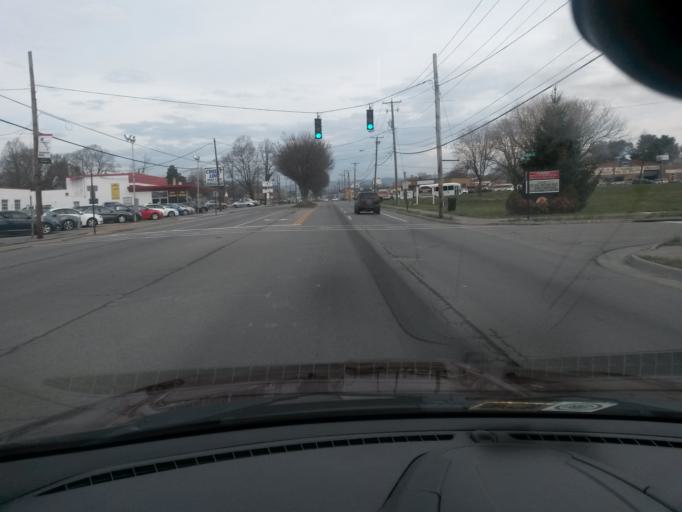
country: US
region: Virginia
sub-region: Roanoke County
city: Hollins
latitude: 37.3081
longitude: -79.9482
